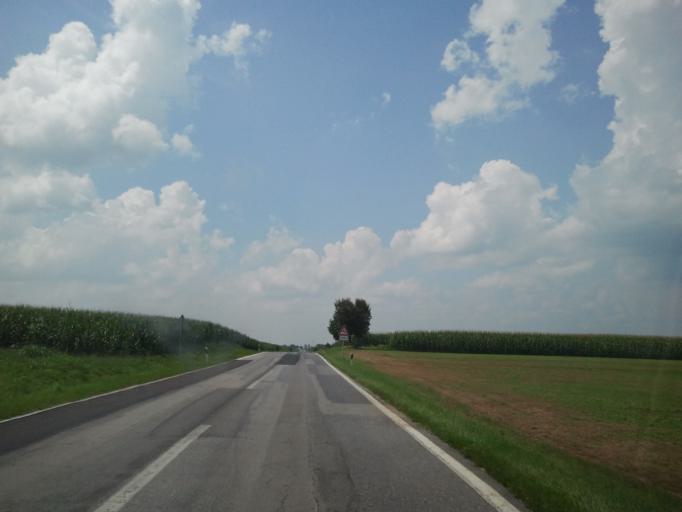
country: HR
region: Vukovarsko-Srijemska
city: Lovas
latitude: 45.2505
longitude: 19.2088
